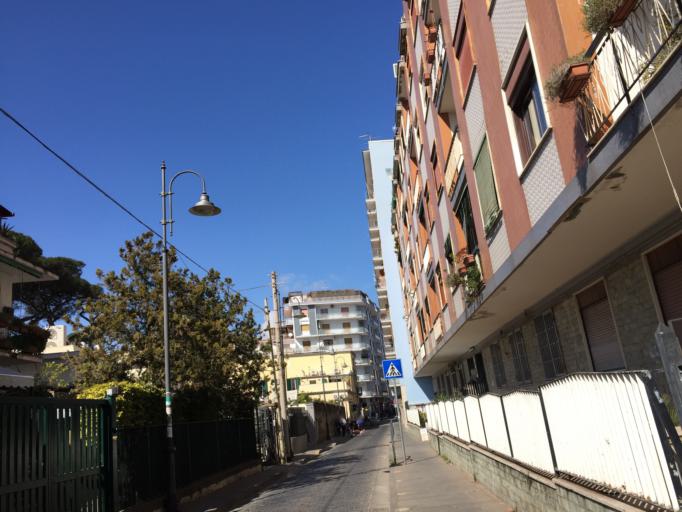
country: IT
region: Campania
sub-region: Provincia di Napoli
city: San Giorgio a Cremano
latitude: 40.8302
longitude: 14.3387
